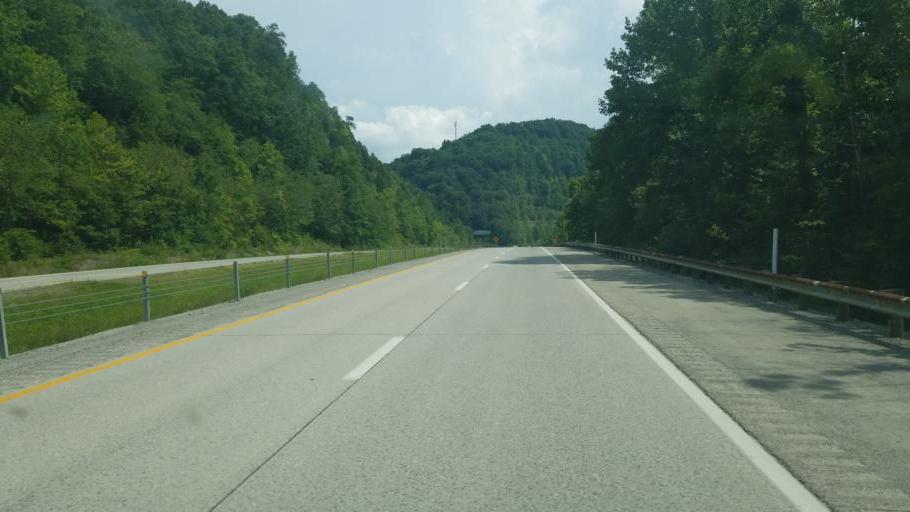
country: US
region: West Virginia
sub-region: Boone County
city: Madison
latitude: 38.1688
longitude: -81.8500
